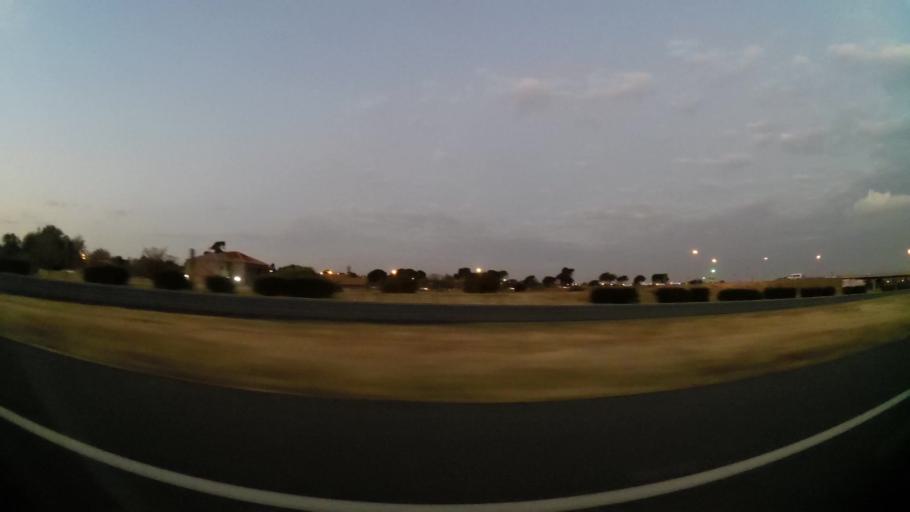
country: ZA
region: Orange Free State
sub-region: Mangaung Metropolitan Municipality
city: Bloemfontein
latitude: -29.1636
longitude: 26.1801
